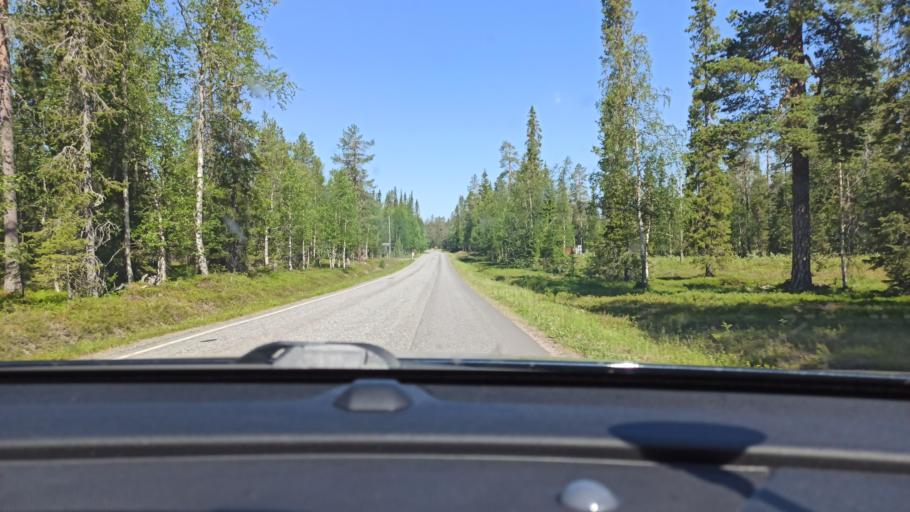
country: FI
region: Lapland
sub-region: Tunturi-Lappi
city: Kolari
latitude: 67.6655
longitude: 24.1612
